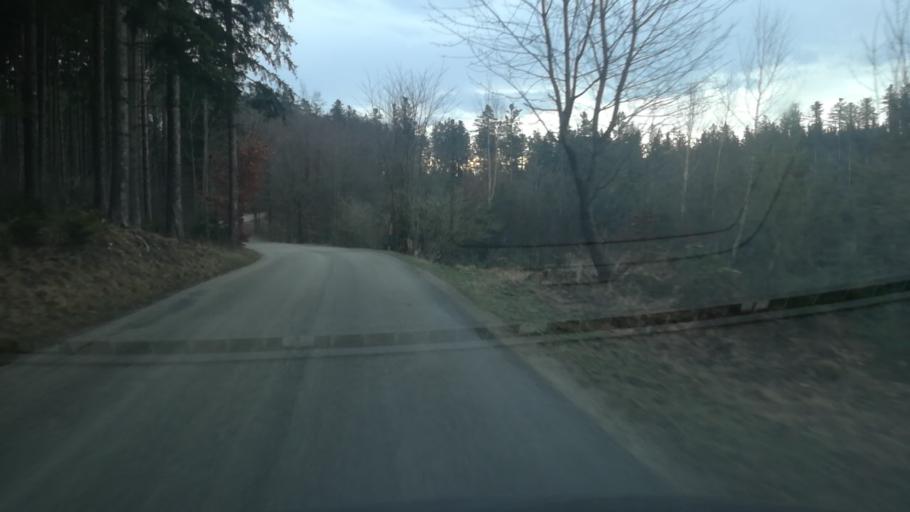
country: AT
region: Upper Austria
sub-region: Politischer Bezirk Vocklabruck
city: Neukirchen an der Vockla
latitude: 48.0590
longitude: 13.5231
